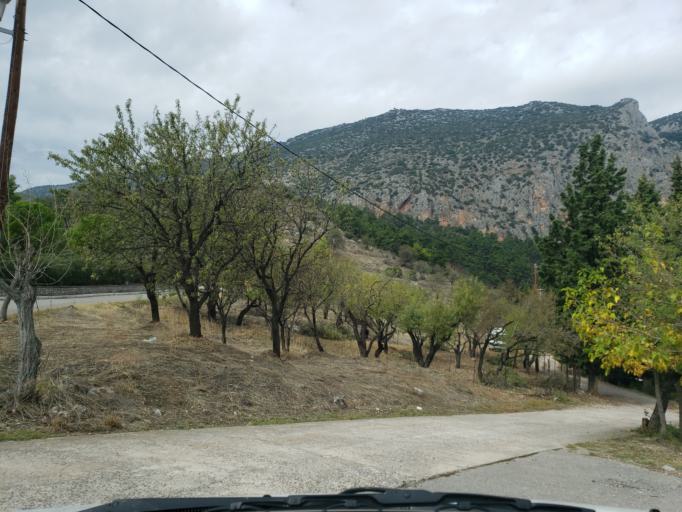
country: GR
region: Central Greece
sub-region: Nomos Fokidos
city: Delphi
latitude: 38.4788
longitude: 22.4980
